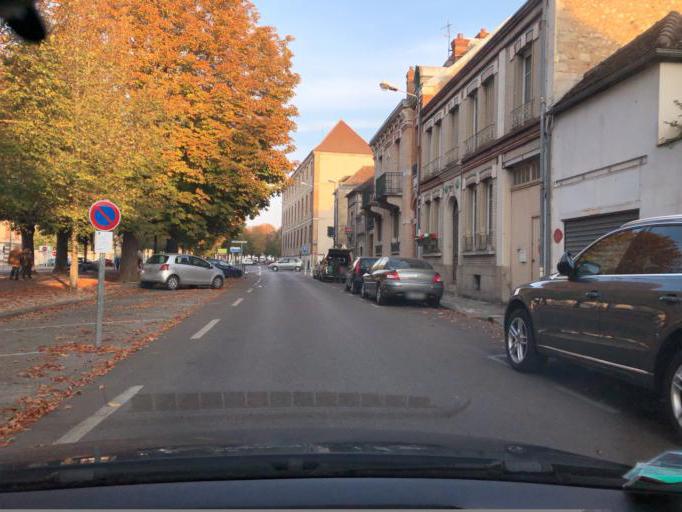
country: FR
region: Bourgogne
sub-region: Departement de l'Yonne
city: Sens
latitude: 48.1993
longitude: 3.2856
